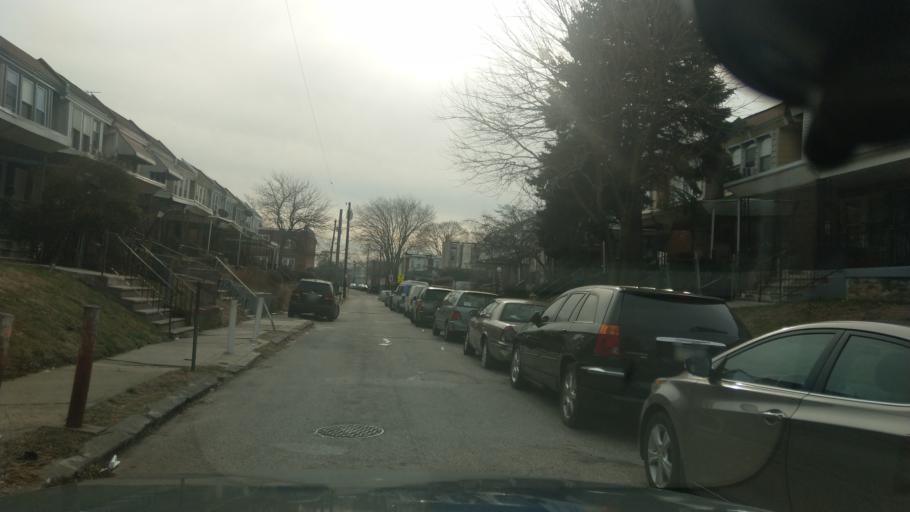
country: US
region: Pennsylvania
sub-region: Montgomery County
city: Wyncote
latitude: 40.0496
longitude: -75.1497
